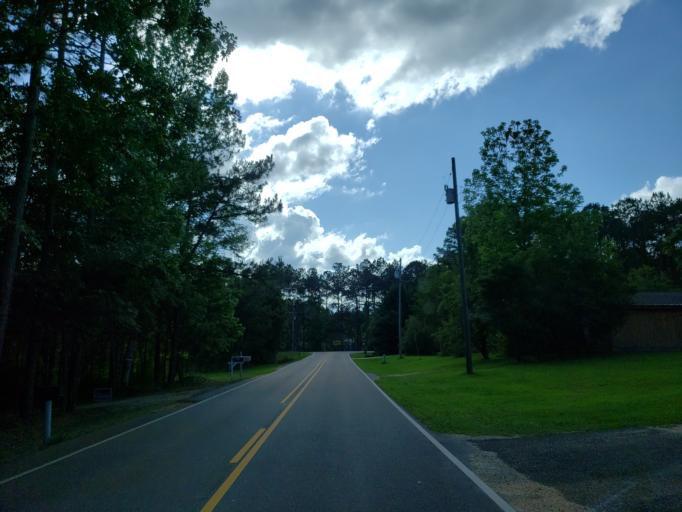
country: US
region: Mississippi
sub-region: Lamar County
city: Sumrall
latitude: 31.3551
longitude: -89.4973
